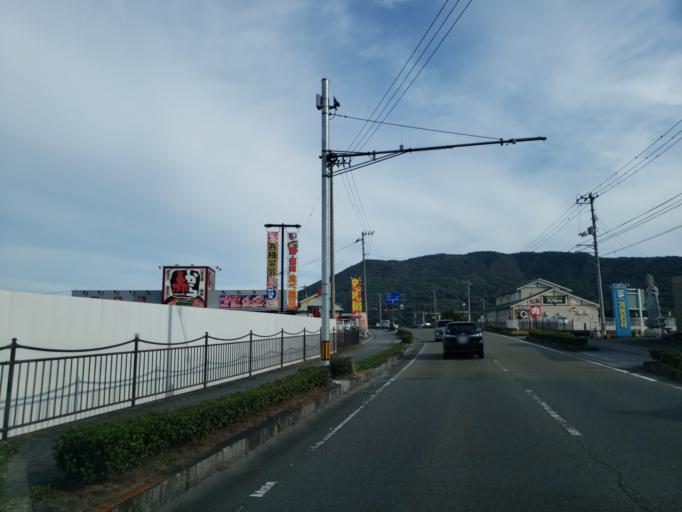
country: JP
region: Tokushima
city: Wakimachi
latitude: 34.0630
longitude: 134.1675
